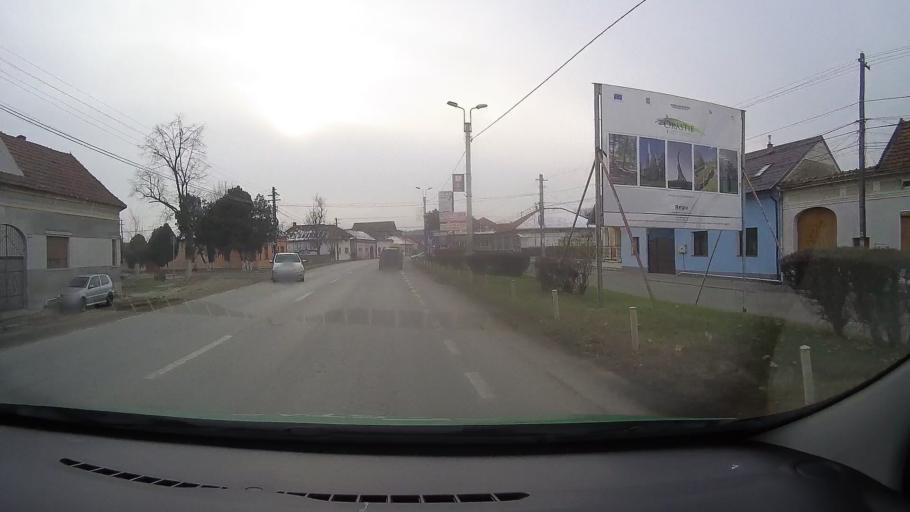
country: RO
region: Hunedoara
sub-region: Municipiul Orastie
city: Orastie
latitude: 45.8469
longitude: 23.2055
